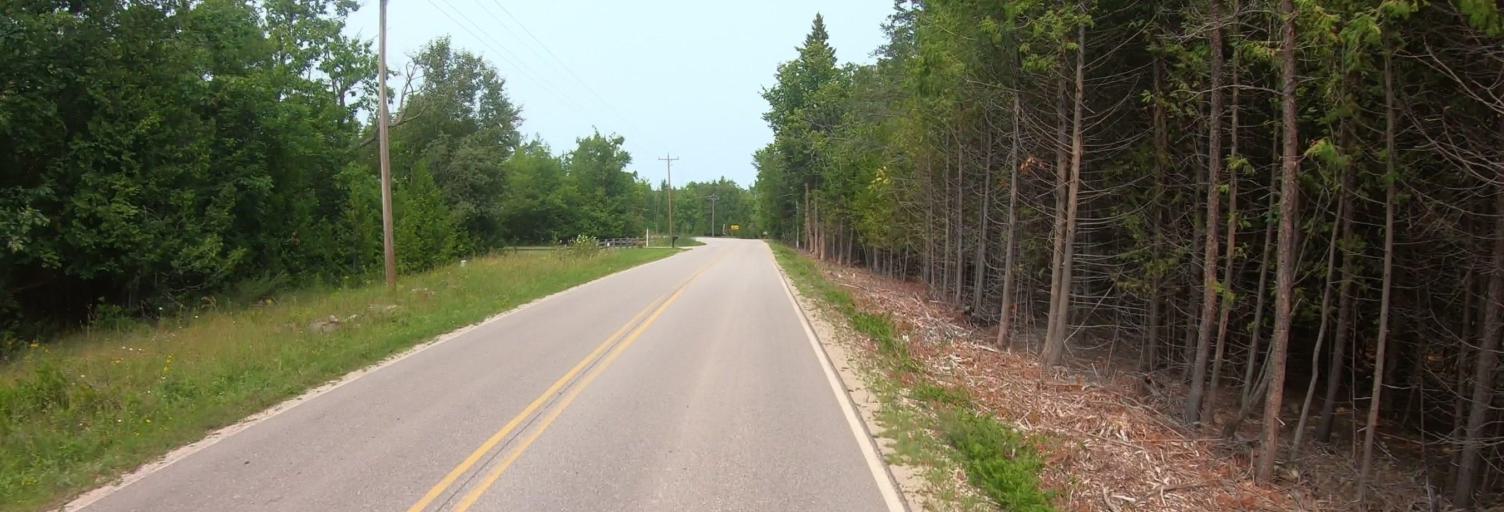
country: CA
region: Ontario
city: Thessalon
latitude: 46.0189
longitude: -83.7182
